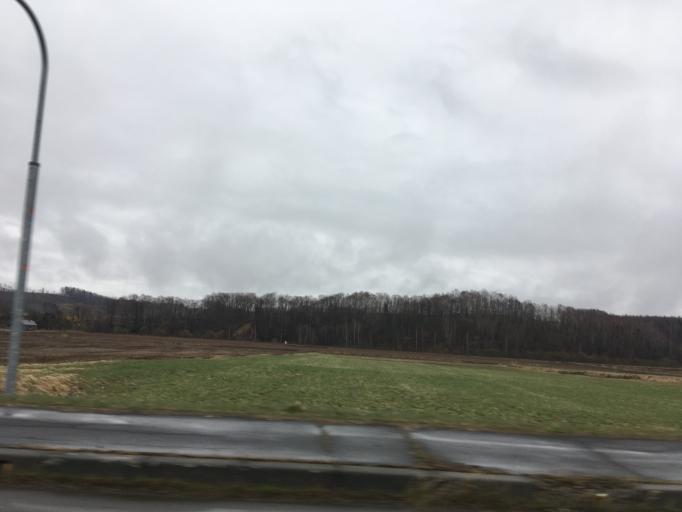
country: JP
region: Hokkaido
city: Nayoro
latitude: 44.0951
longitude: 142.4739
